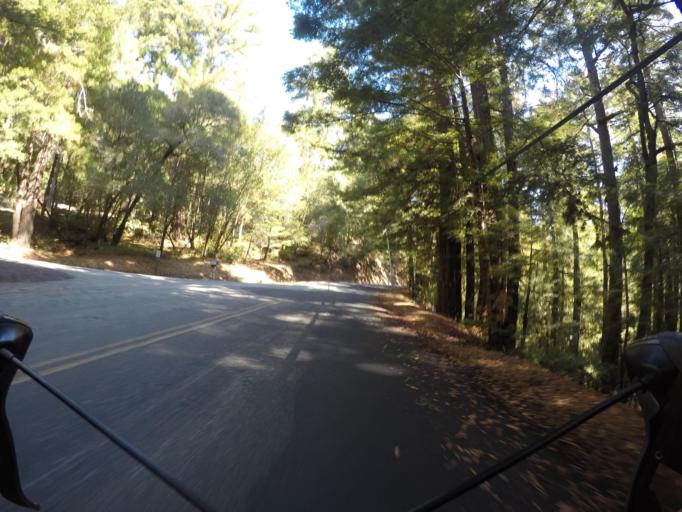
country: US
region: California
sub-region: San Mateo County
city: Portola Valley
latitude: 37.2745
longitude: -122.3012
